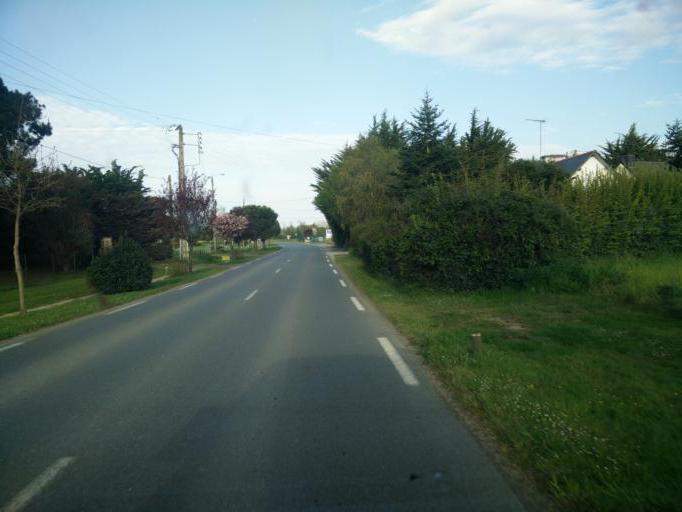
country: FR
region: Brittany
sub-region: Departement des Cotes-d'Armor
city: Plurien
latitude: 48.6271
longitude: -2.3732
